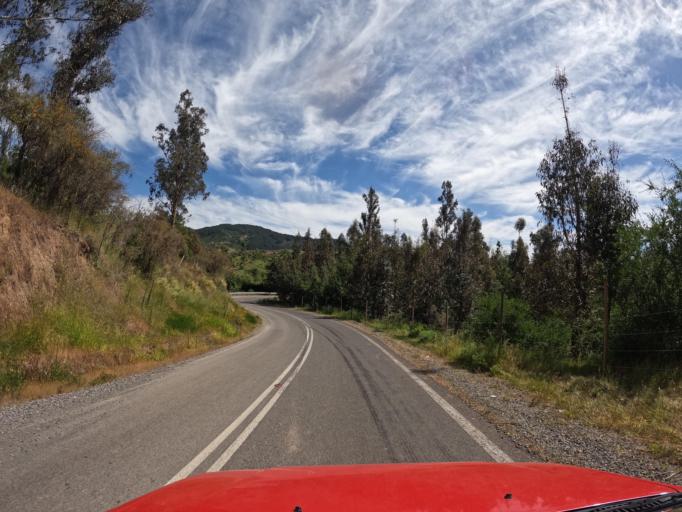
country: CL
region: Maule
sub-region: Provincia de Talca
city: Talca
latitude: -34.9918
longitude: -71.8536
